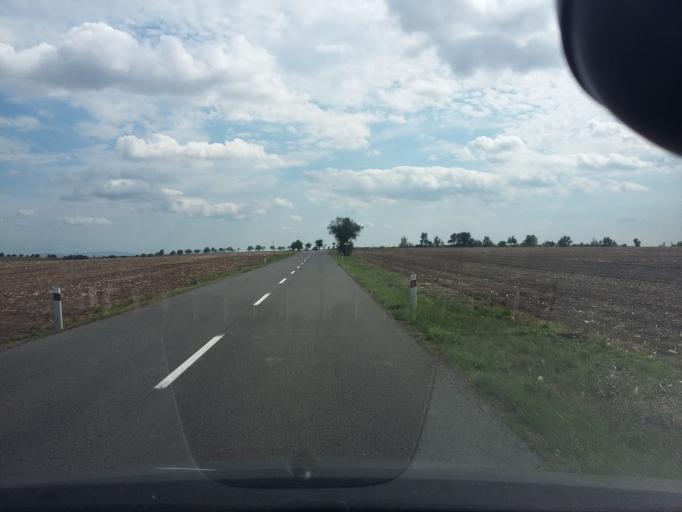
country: SK
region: Trnavsky
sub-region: Okres Skalica
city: Holic
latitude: 48.7688
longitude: 17.1736
